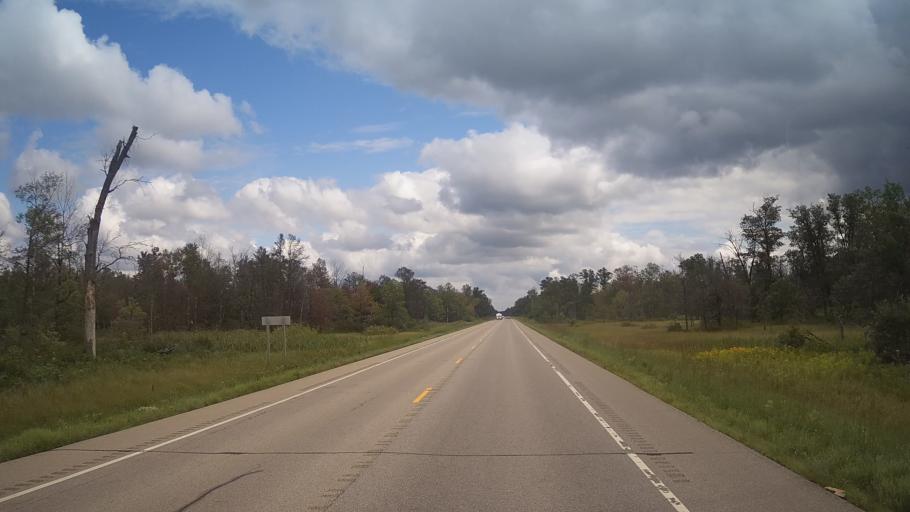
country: US
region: Wisconsin
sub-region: Adams County
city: Friendship
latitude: 44.0253
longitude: -89.7257
